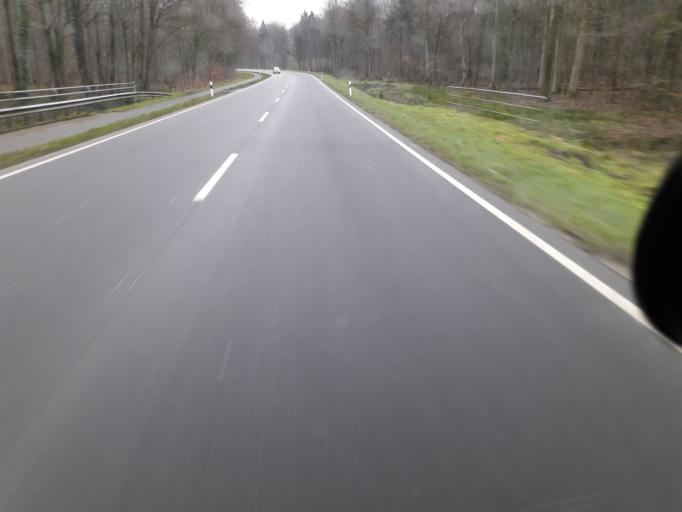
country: DE
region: Lower Saxony
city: Bad Bentheim
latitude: 52.3231
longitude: 7.1547
